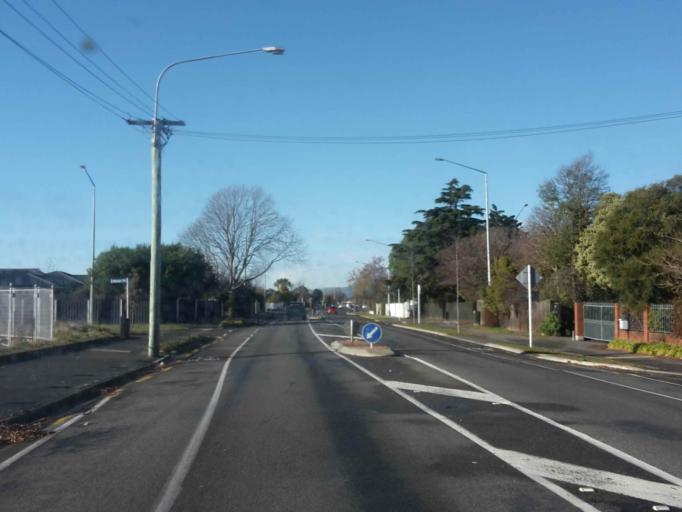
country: NZ
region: Canterbury
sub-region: Christchurch City
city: Christchurch
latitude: -43.5008
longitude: 172.5888
